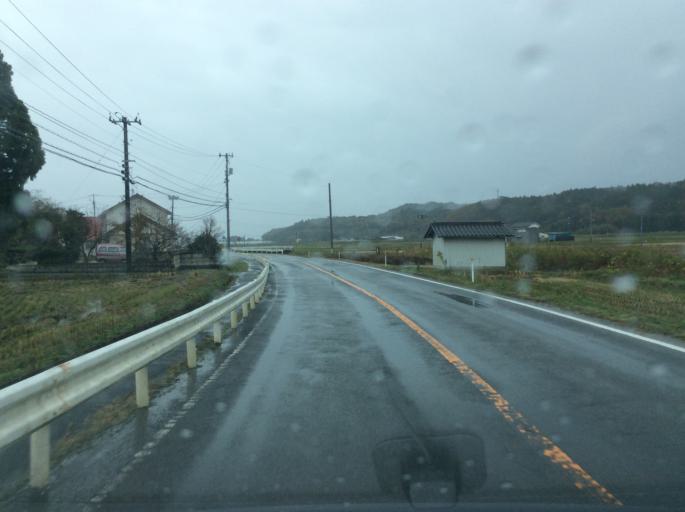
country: JP
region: Fukushima
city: Iwaki
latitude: 37.1134
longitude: 140.9328
